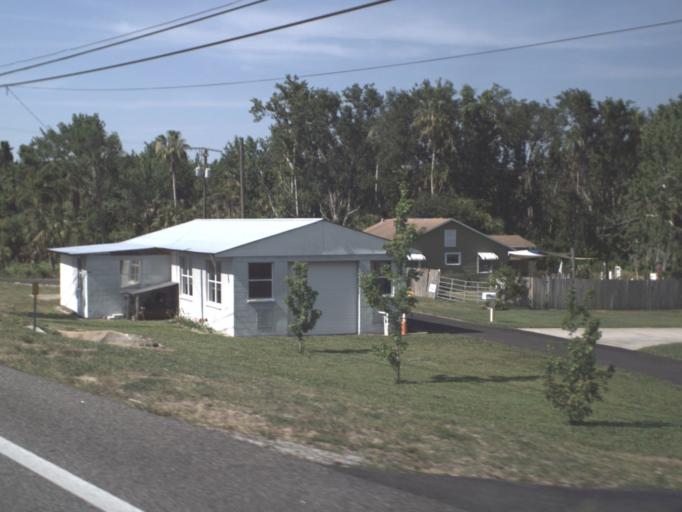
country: US
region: Florida
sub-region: Brevard County
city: Sharpes
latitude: 28.4291
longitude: -80.7590
